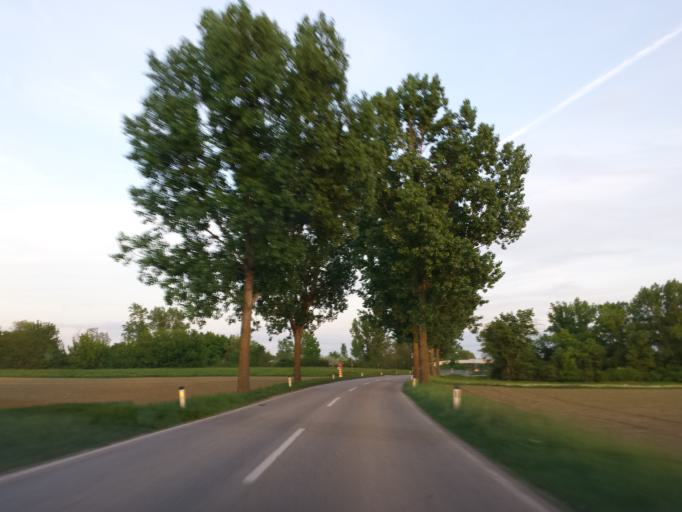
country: AT
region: Lower Austria
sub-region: Politischer Bezirk Tulln
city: Michelhausen
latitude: 48.3375
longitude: 15.9381
